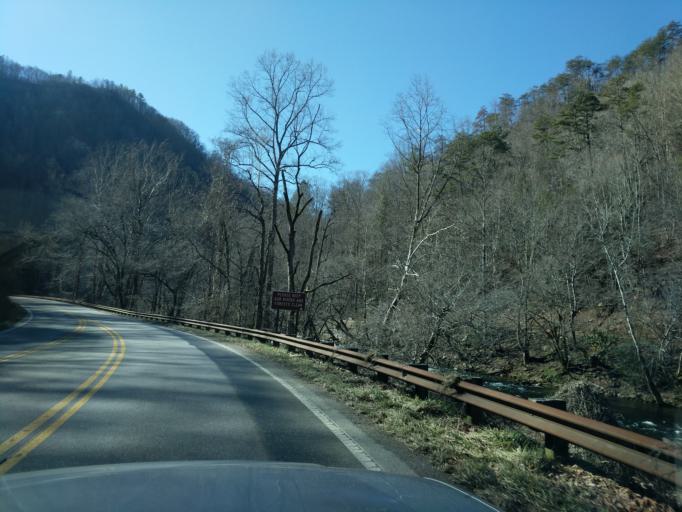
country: US
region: North Carolina
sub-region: Swain County
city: Bryson City
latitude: 35.3332
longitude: -83.5972
